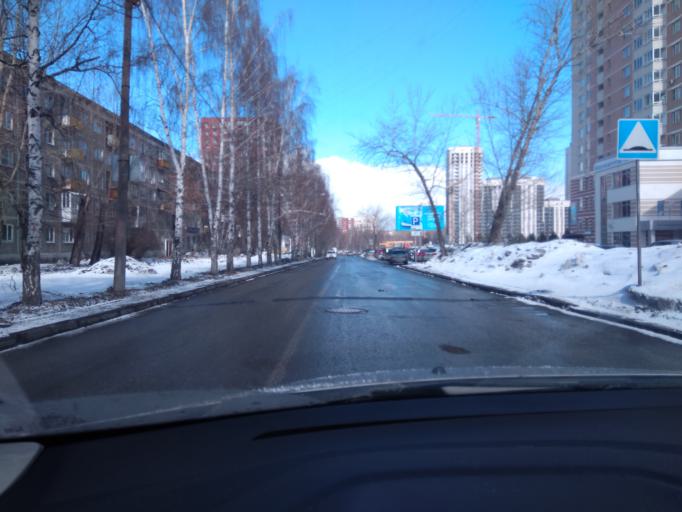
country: RU
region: Sverdlovsk
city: Sovkhoznyy
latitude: 56.8109
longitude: 60.5658
